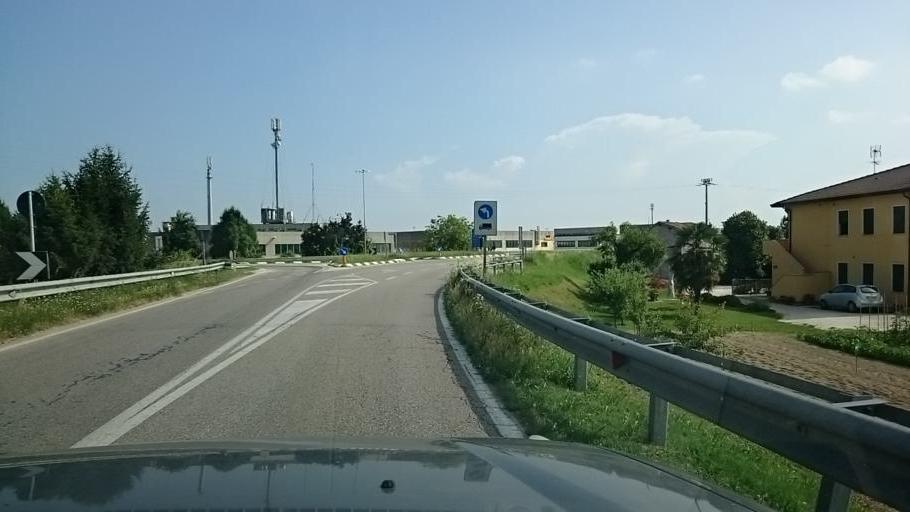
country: IT
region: Veneto
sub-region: Provincia di Padova
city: Tavo
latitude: 45.4876
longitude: 11.8570
